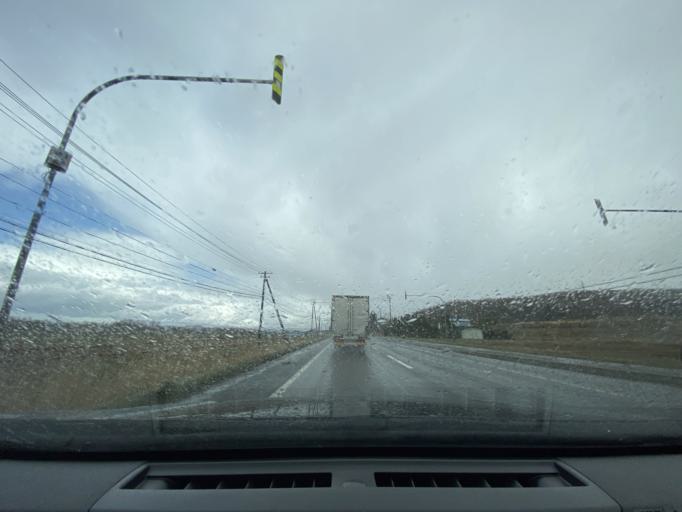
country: JP
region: Hokkaido
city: Fukagawa
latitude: 43.6755
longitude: 142.0256
